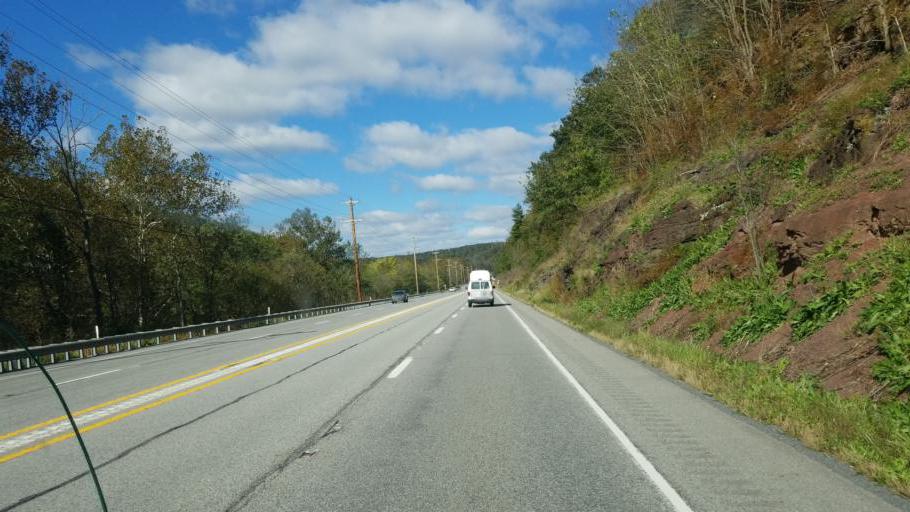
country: US
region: Pennsylvania
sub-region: Bedford County
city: Earlston
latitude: 40.0004
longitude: -78.2940
